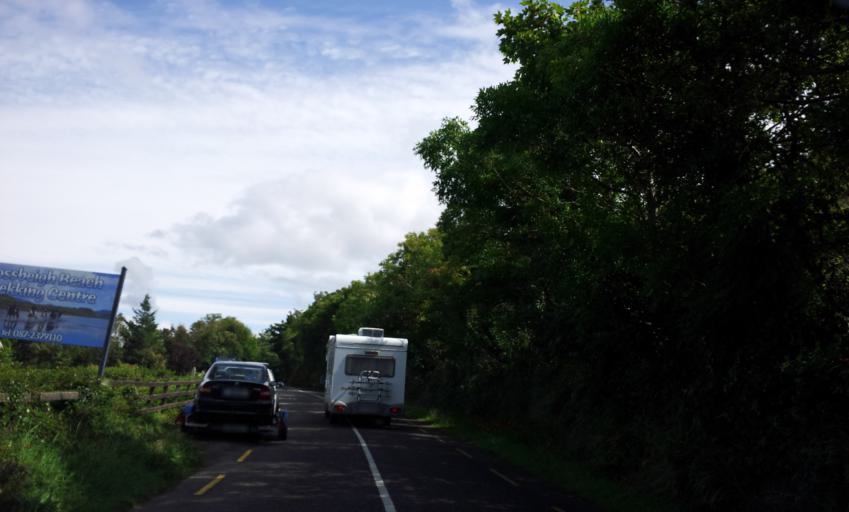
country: IE
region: Munster
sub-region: Ciarrai
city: Killorglin
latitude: 52.0560
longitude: -9.9567
